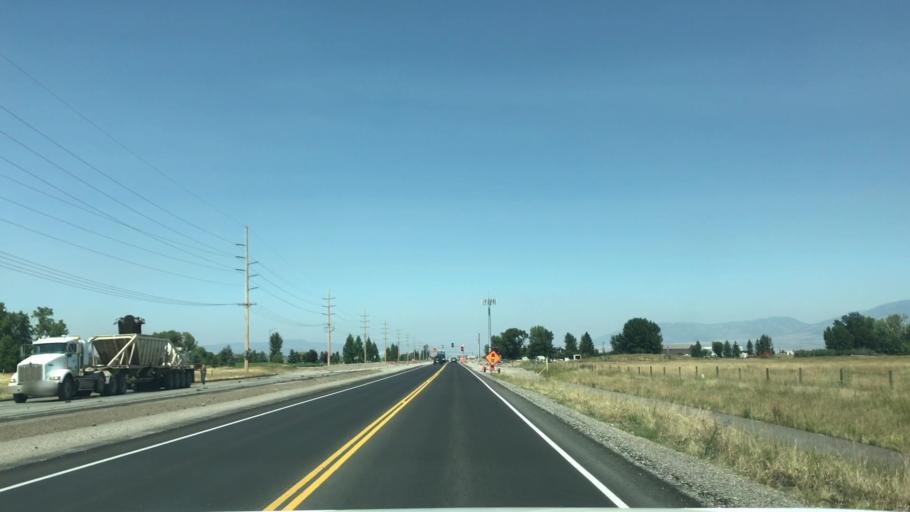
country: US
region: Montana
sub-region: Gallatin County
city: Belgrade
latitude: 45.7190
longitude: -111.1851
